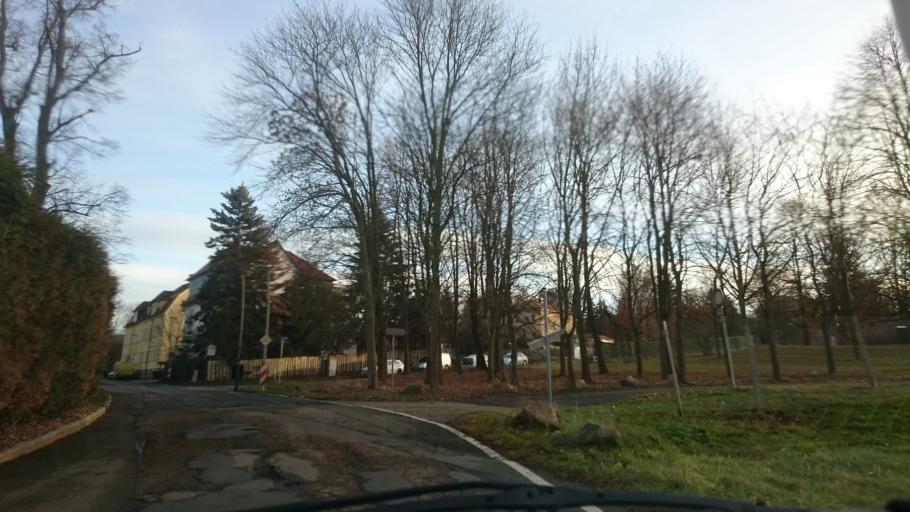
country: DE
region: Saxony
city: Zwickau
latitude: 50.7388
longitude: 12.5177
